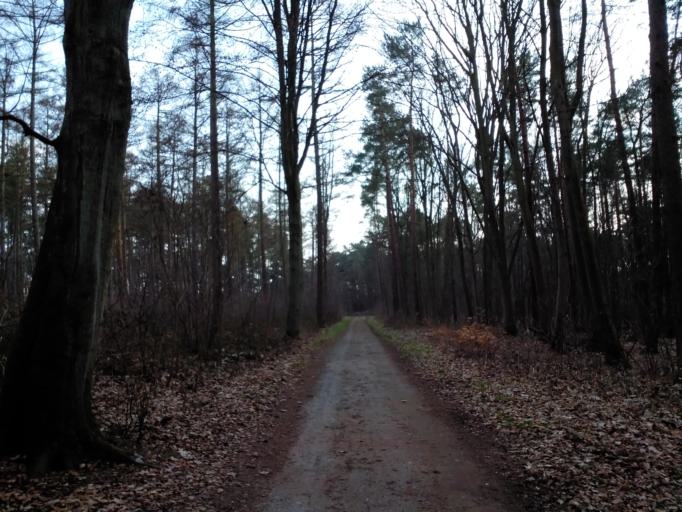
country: BE
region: Flanders
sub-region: Provincie Vlaams-Brabant
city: Oud-Heverlee
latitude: 50.8323
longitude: 4.6890
